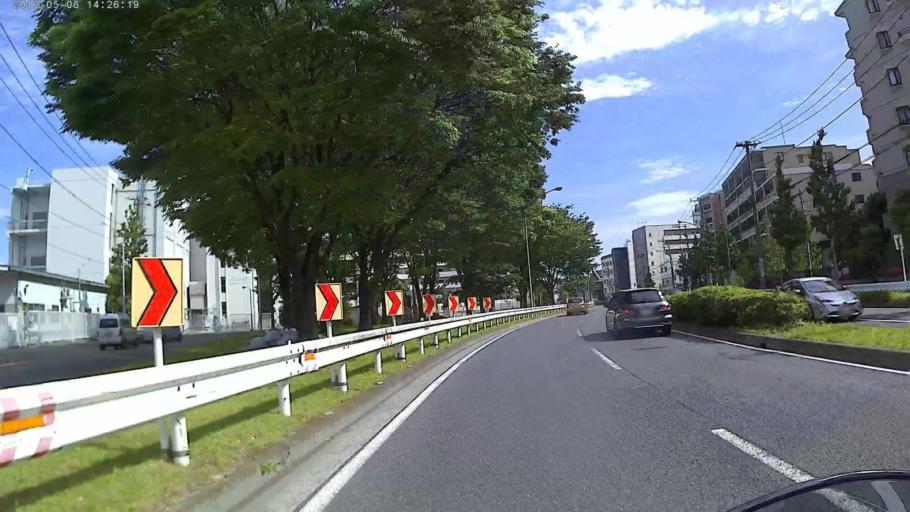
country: JP
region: Kanagawa
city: Yokohama
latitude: 35.4357
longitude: 139.6627
